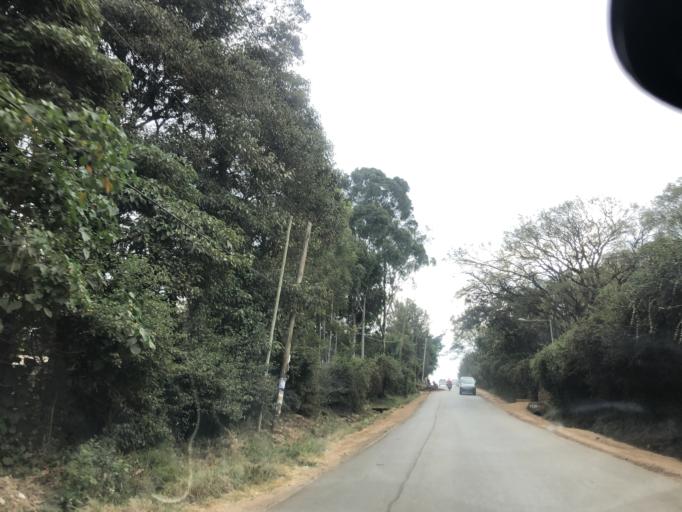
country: KE
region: Kiambu
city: Kiambu
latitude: -1.2124
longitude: 36.8911
